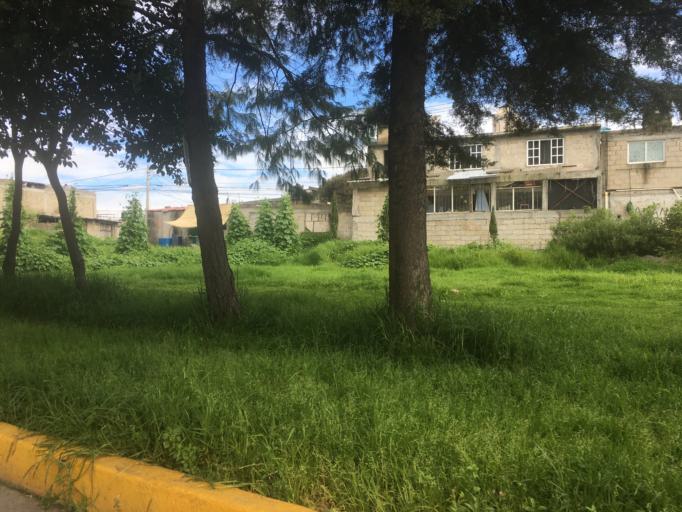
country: MX
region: Mexico
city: Santa Maria Totoltepec
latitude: 19.3030
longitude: -99.5916
